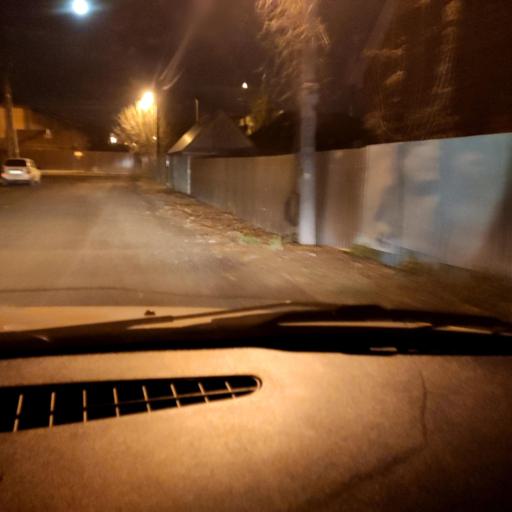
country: RU
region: Bashkortostan
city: Ufa
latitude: 54.7051
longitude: 55.9460
